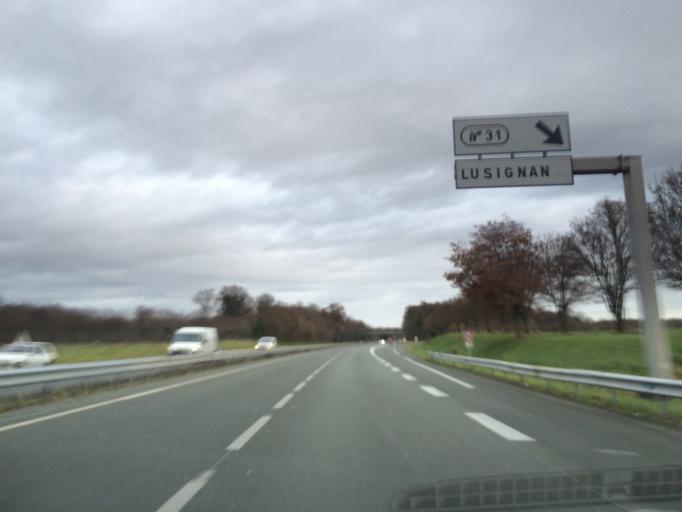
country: FR
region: Poitou-Charentes
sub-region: Departement des Deux-Sevres
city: Pamproux
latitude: 46.4274
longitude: -0.0875
